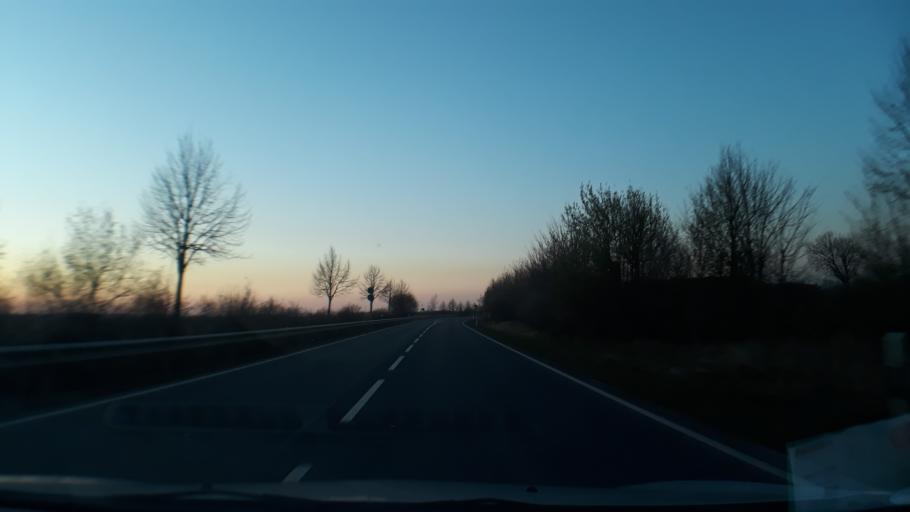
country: DE
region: North Rhine-Westphalia
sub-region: Regierungsbezirk Koln
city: Norvenich
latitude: 50.8317
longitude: 6.6273
